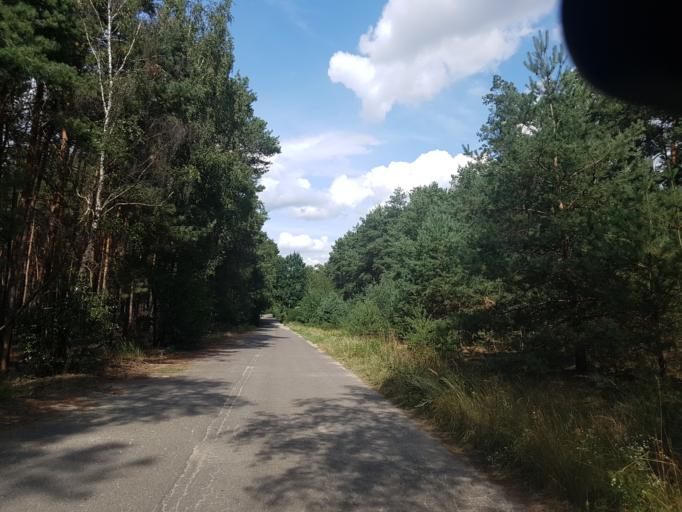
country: DE
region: Brandenburg
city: Schonborn
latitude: 51.6598
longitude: 13.5002
